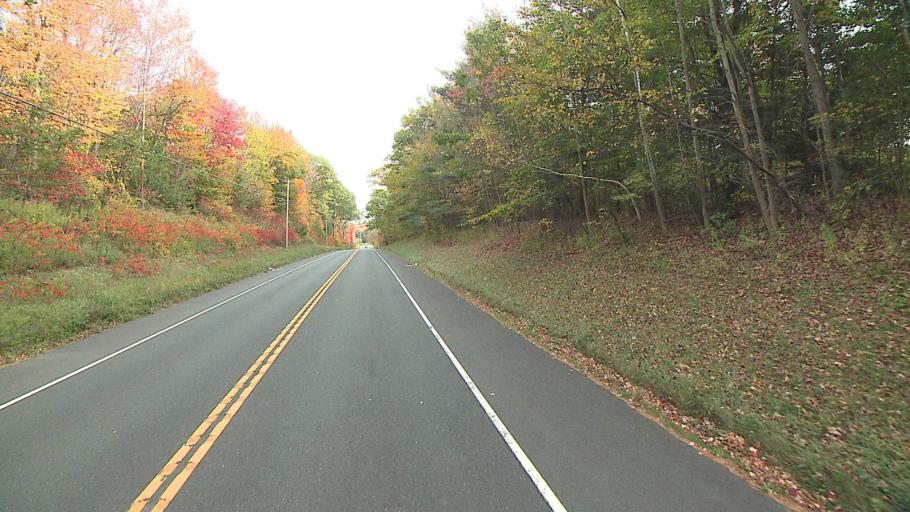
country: US
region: Connecticut
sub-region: Litchfield County
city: Winchester Center
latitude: 41.9777
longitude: -73.1490
